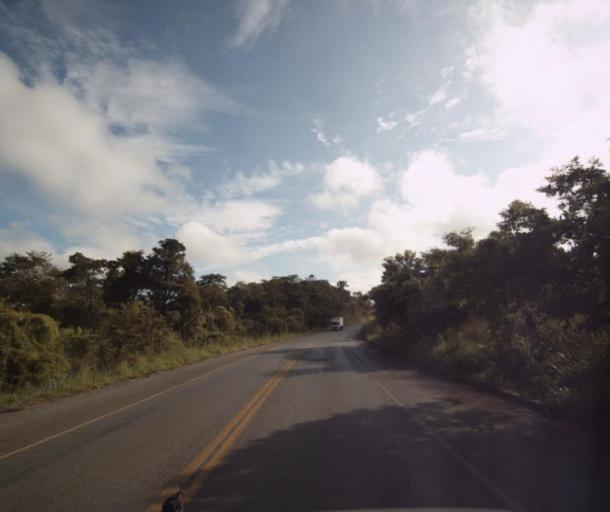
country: BR
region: Goias
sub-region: Padre Bernardo
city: Padre Bernardo
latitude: -15.4870
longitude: -48.6186
